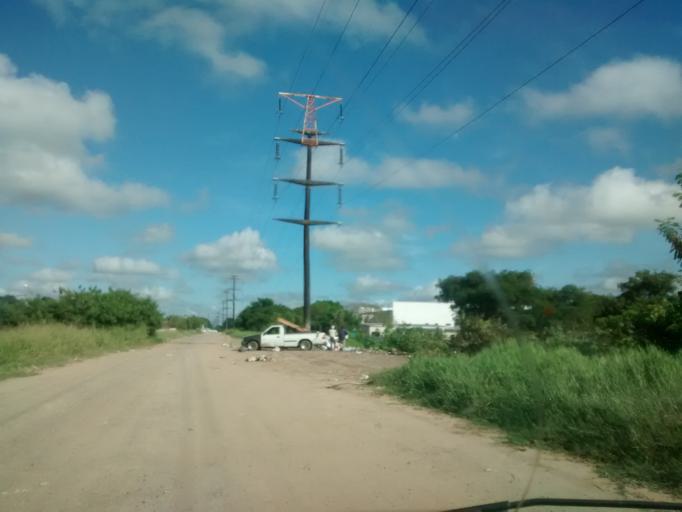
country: AR
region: Chaco
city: Resistencia
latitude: -27.4341
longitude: -58.9628
